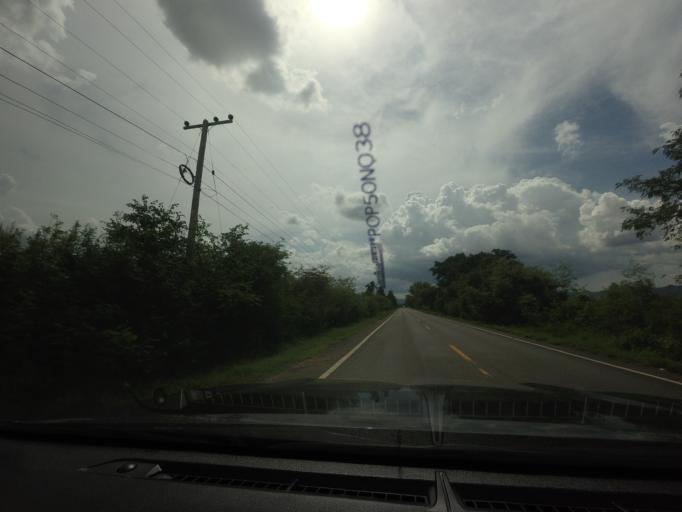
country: TH
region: Kanchanaburi
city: Bo Phloi
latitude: 14.1664
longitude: 99.4501
